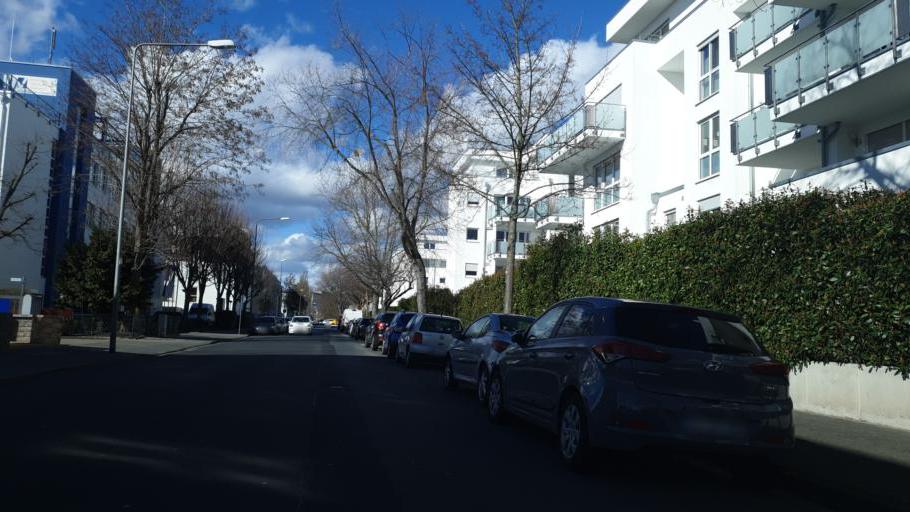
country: DE
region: Hesse
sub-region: Regierungsbezirk Darmstadt
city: Wiesbaden
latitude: 50.0616
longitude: 8.2583
